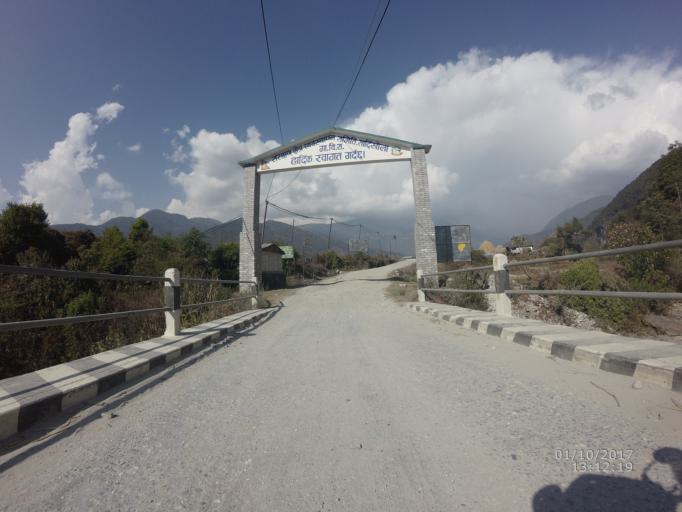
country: NP
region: Western Region
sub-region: Gandaki Zone
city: Pokhara
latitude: 28.3155
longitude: 83.9617
